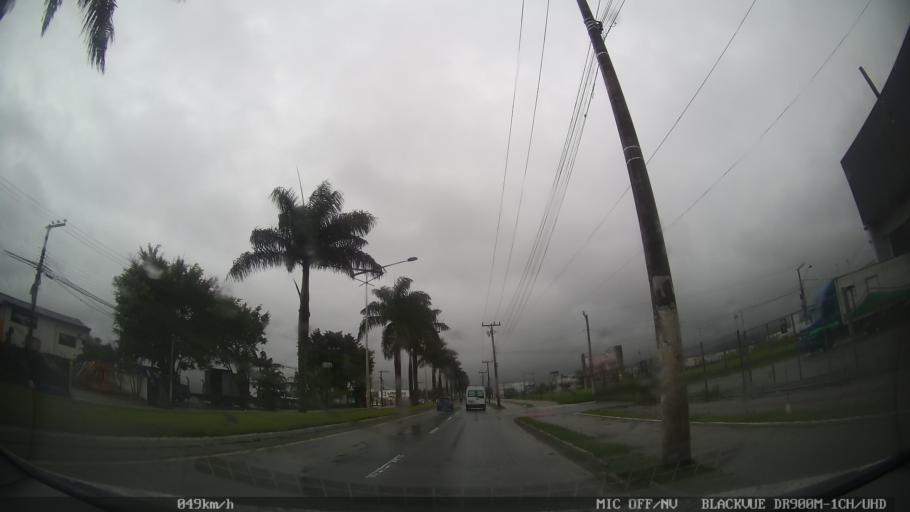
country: BR
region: Santa Catarina
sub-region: Itajai
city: Itajai
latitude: -26.9167
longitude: -48.7042
